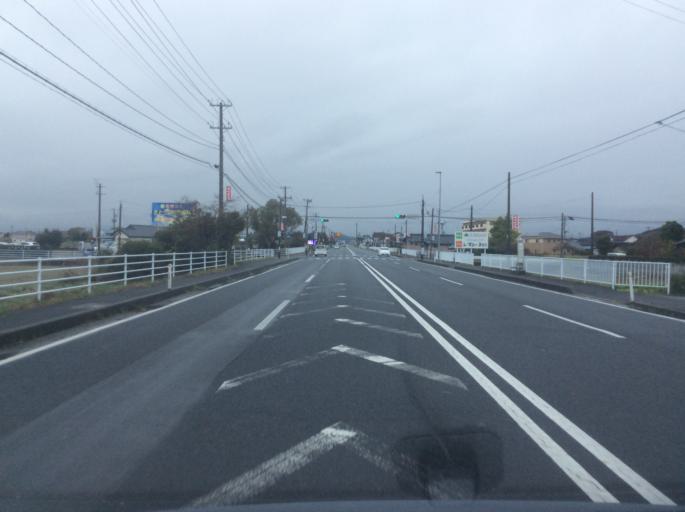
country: JP
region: Fukushima
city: Iwaki
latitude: 37.0895
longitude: 140.9712
